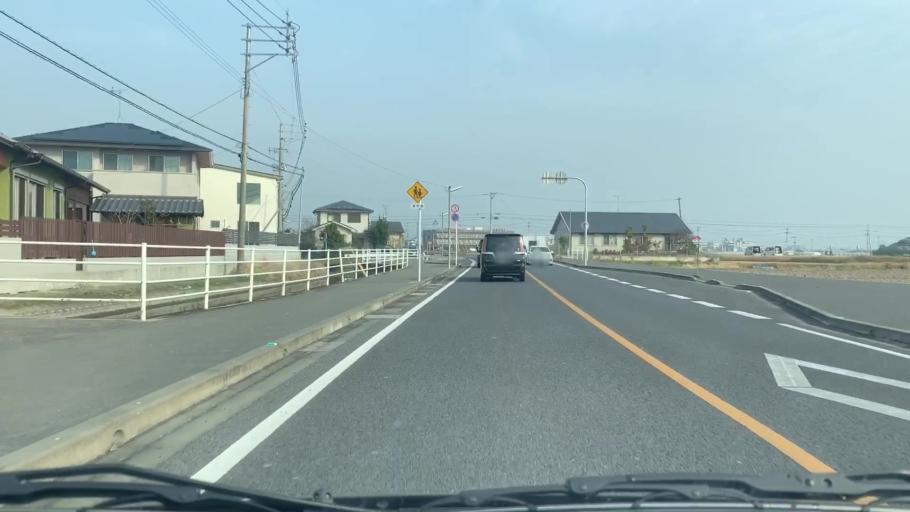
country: JP
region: Saga Prefecture
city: Saga-shi
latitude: 33.2352
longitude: 130.2577
